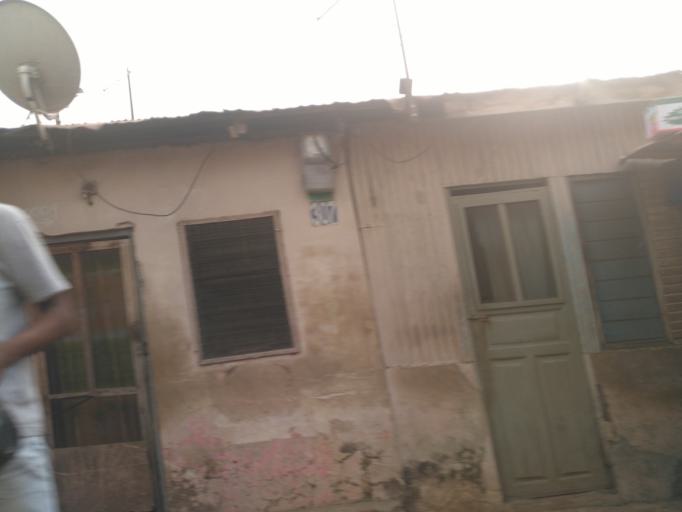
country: GH
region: Ashanti
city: Kumasi
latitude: 6.6787
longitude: -1.5911
